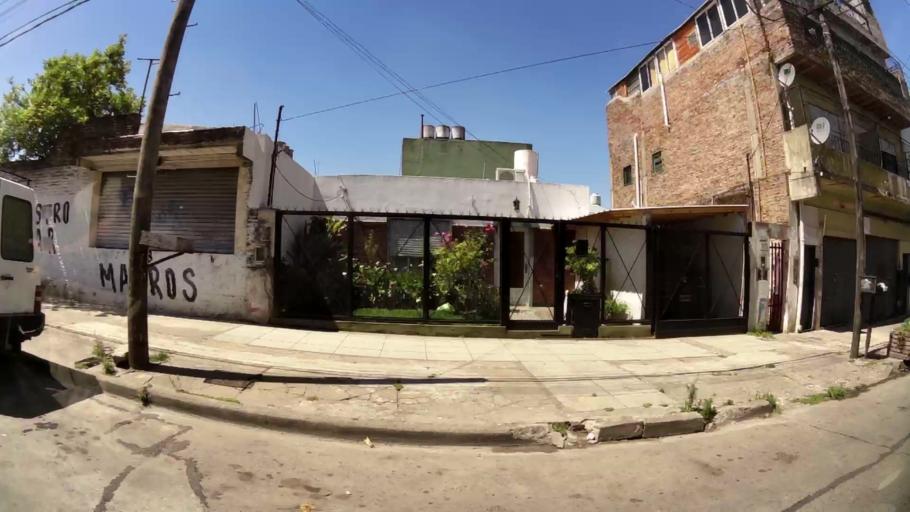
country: AR
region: Buenos Aires
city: Caseros
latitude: -34.5678
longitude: -58.5759
